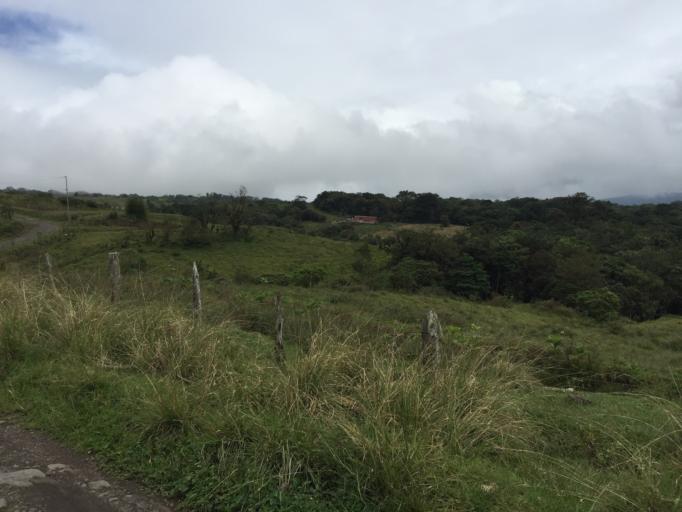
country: CR
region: Heredia
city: Angeles
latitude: 10.0398
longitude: -83.9894
